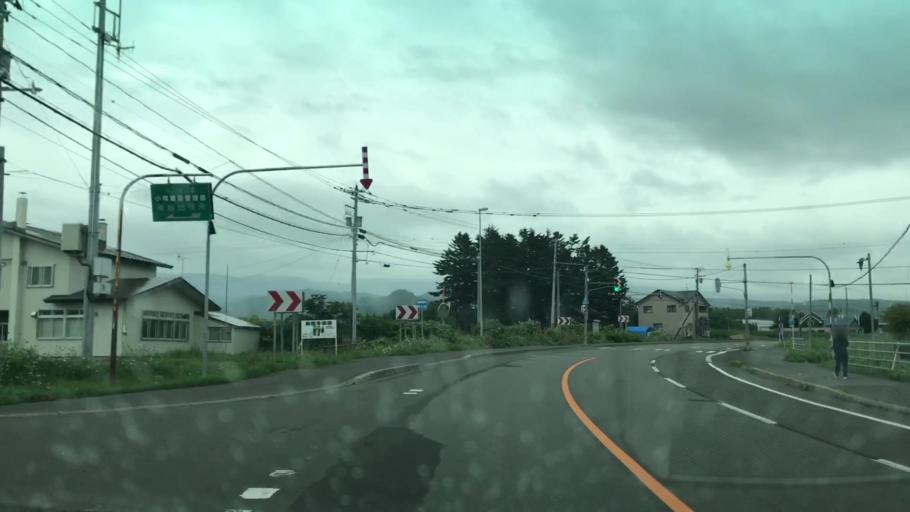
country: JP
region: Hokkaido
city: Niseko Town
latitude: 42.8131
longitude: 140.5442
